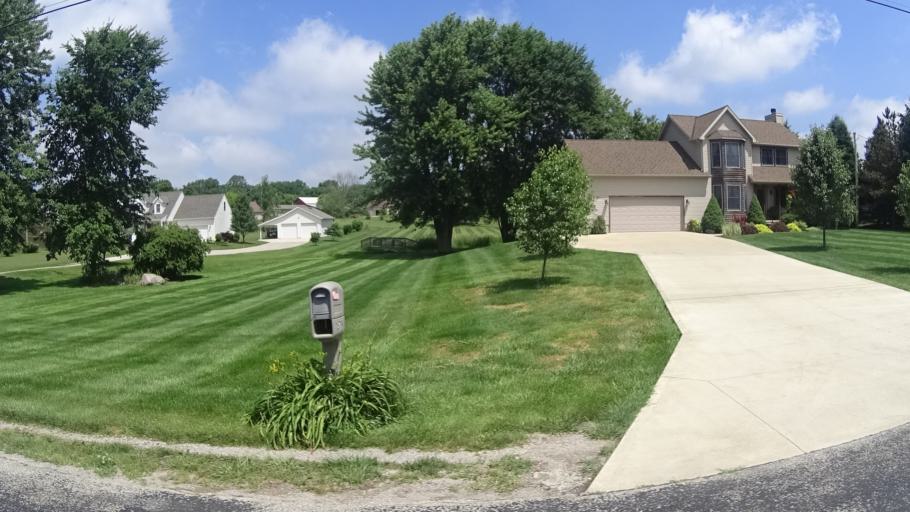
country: US
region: Ohio
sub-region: Huron County
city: Wakeman
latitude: 41.3204
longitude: -82.3474
